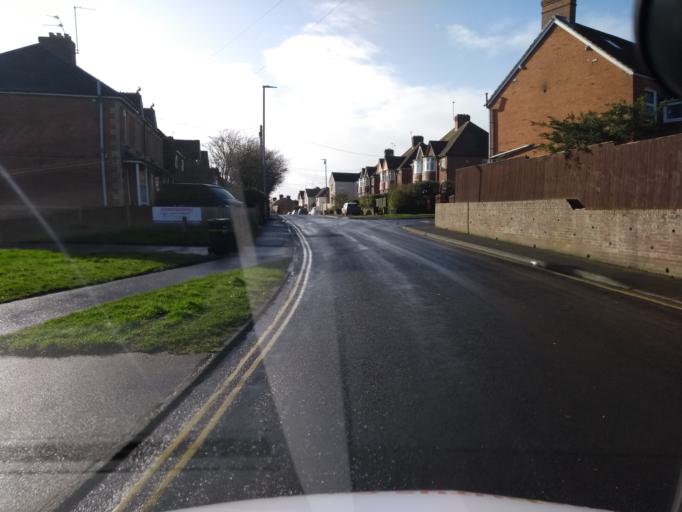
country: GB
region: England
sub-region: Somerset
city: Yeovil
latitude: 50.9509
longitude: -2.6222
